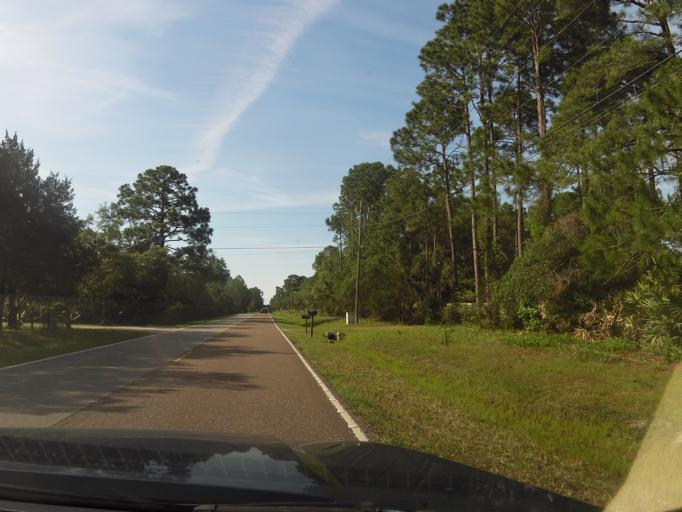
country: US
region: Florida
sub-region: Duval County
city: Atlantic Beach
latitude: 30.4782
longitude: -81.4705
